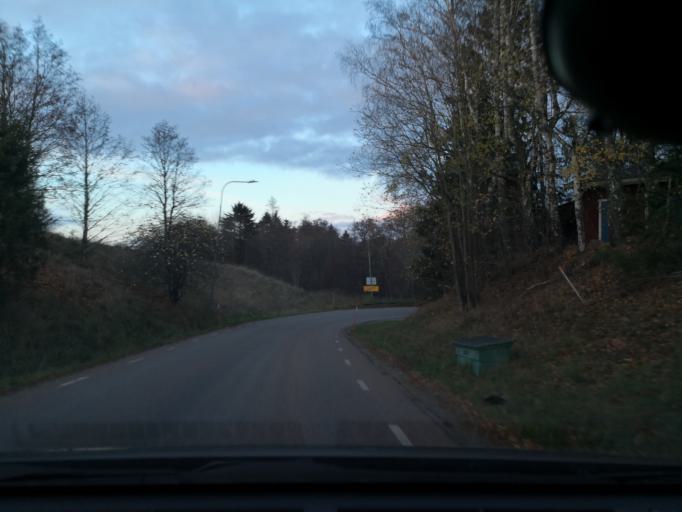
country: SE
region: Uppsala
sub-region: Enkopings Kommun
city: Irsta
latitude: 59.6793
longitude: 16.8383
